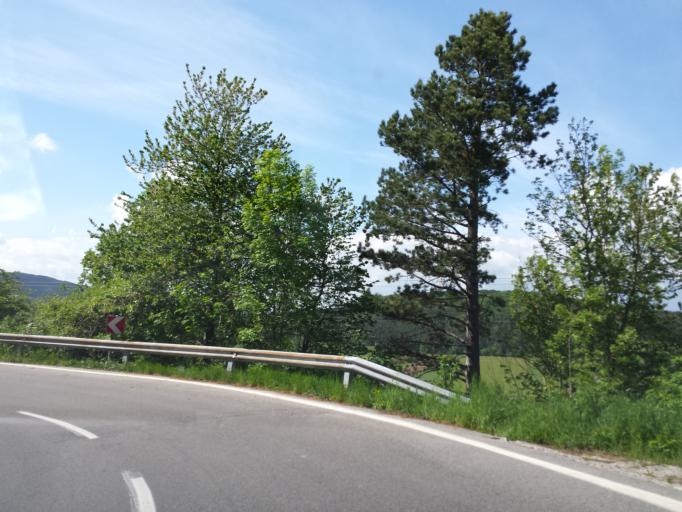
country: AT
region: Lower Austria
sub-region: Politischer Bezirk Baden
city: Hernstein
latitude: 47.8907
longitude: 16.1124
